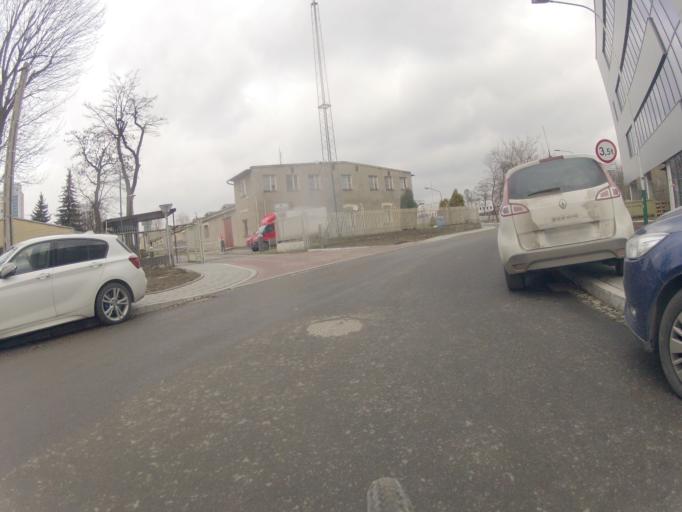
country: PL
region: Lesser Poland Voivodeship
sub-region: Krakow
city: Krakow
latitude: 50.0658
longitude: 19.9813
